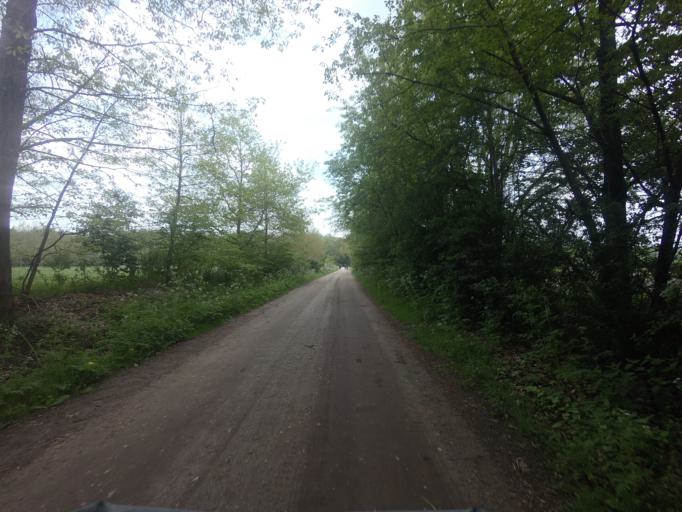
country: NL
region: Overijssel
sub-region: Gemeente Hof van Twente
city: Delden
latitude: 52.2468
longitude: 6.7207
